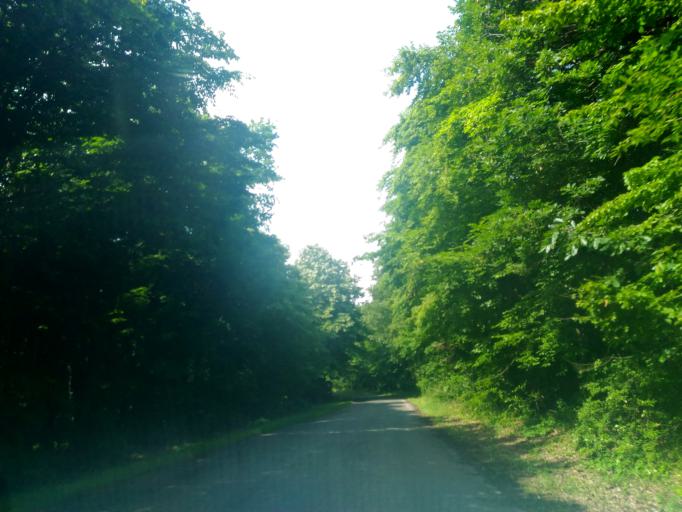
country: HU
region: Baranya
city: Pecs
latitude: 46.1219
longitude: 18.2127
